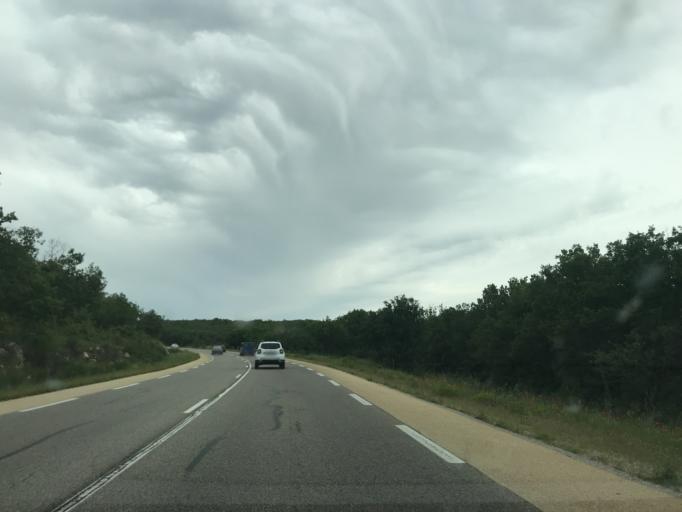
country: FR
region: Provence-Alpes-Cote d'Azur
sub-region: Departement du Var
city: Pourrieres
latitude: 43.5383
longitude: 5.8118
